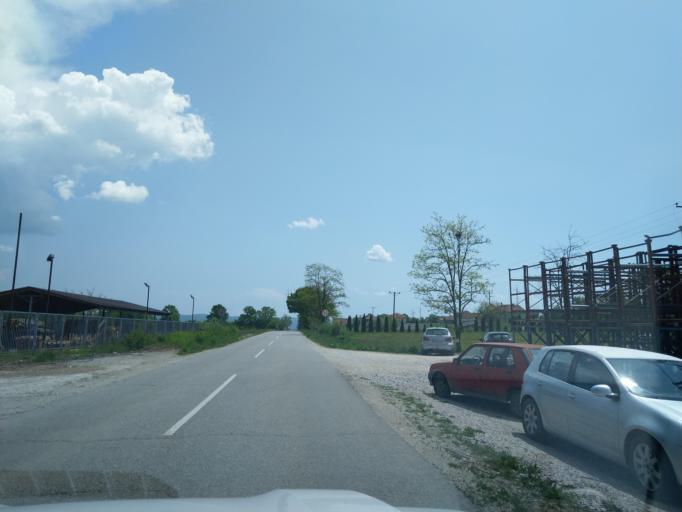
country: RS
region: Central Serbia
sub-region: Zlatiborski Okrug
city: Pozega
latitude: 43.8545
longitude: 19.9889
